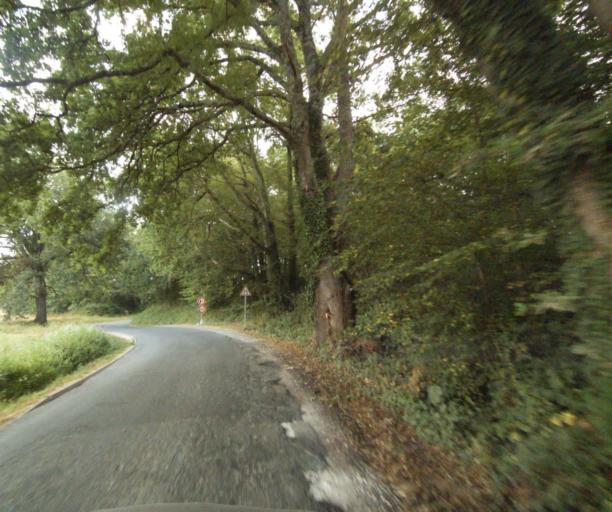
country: FR
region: Aquitaine
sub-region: Departement de la Gironde
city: La Sauve
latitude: 44.7821
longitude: -0.3217
